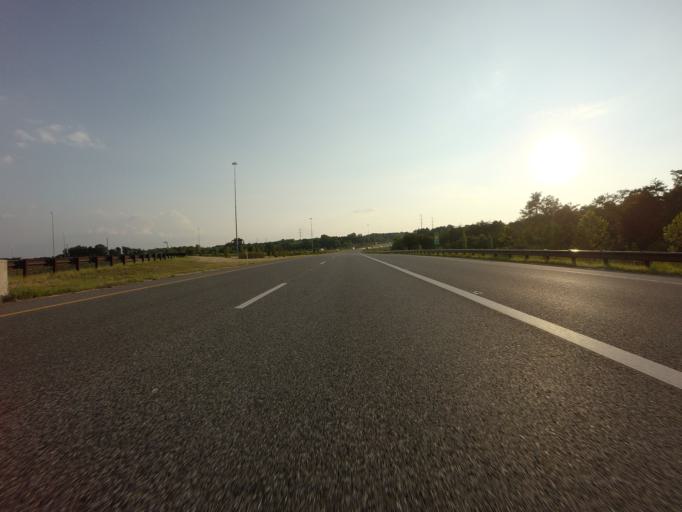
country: US
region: Maryland
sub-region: Prince George's County
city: West Laurel
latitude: 39.0761
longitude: -76.9073
